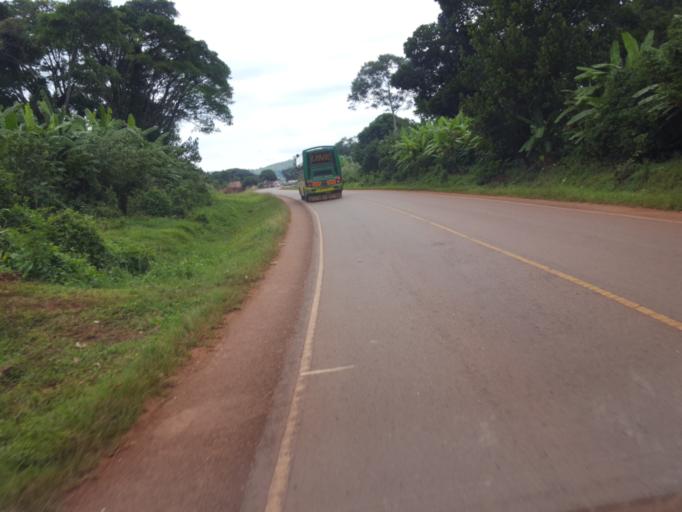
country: UG
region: Central Region
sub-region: Mityana District
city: Mityana
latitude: 0.6652
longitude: 32.0885
